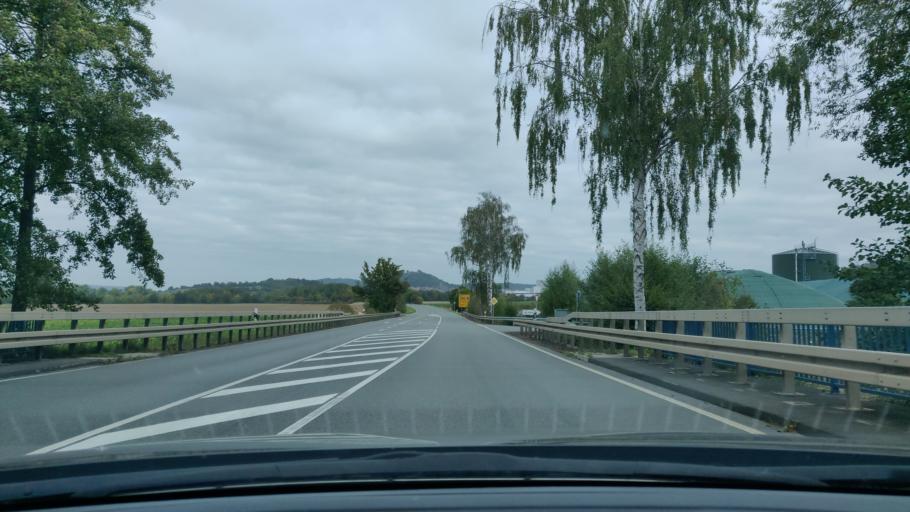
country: DE
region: Hesse
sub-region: Regierungsbezirk Kassel
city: Homberg
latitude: 51.0115
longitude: 9.3751
